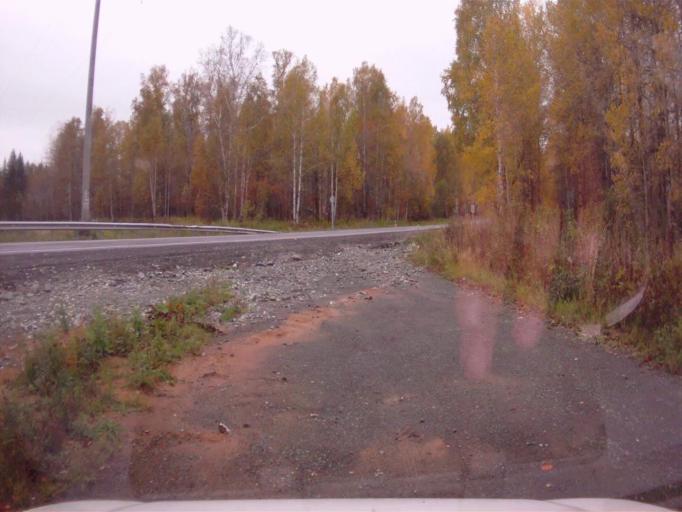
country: RU
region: Chelyabinsk
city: Nyazepetrovsk
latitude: 56.0659
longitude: 59.6532
